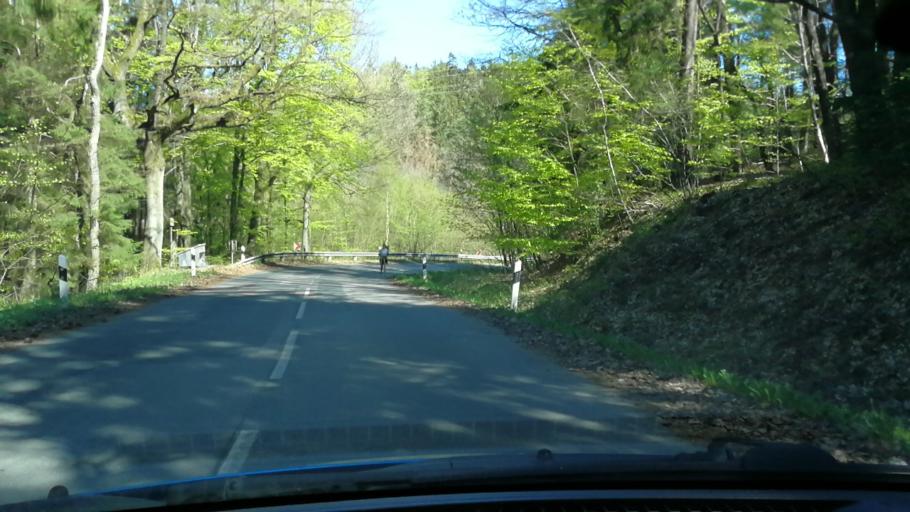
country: DE
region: Lower Saxony
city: Adelebsen
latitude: 51.6422
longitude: 9.7674
